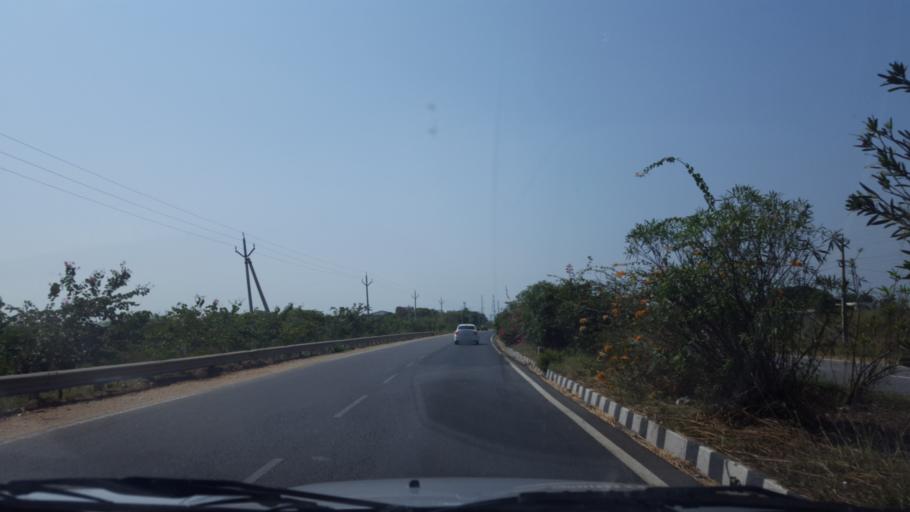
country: IN
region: Andhra Pradesh
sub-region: Guntur
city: Chilakalurupet
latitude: 16.0557
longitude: 80.1462
